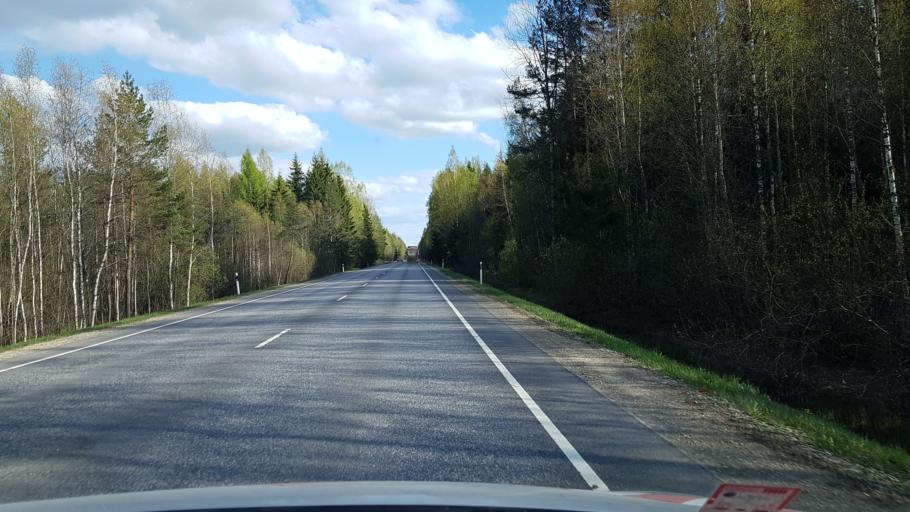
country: EE
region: Vorumaa
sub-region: Antsla vald
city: Vana-Antsla
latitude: 58.0228
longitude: 26.7420
